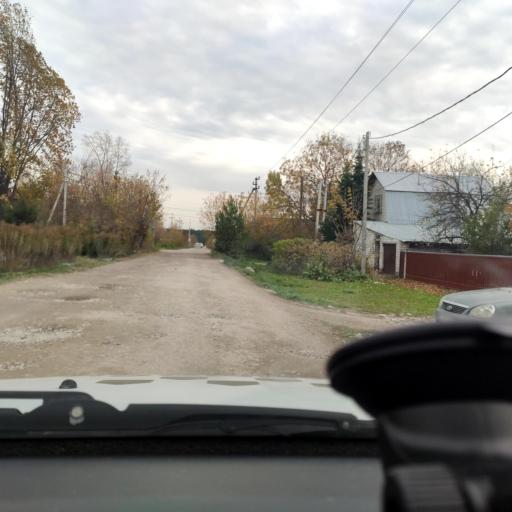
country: RU
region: Perm
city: Perm
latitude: 57.9910
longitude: 56.3030
